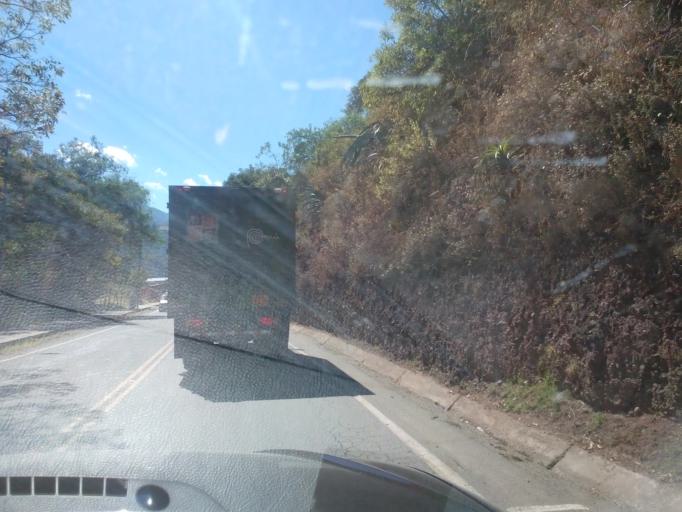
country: PE
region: Cusco
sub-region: Provincia de Anta
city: Limatambo
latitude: -13.4767
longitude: -72.4406
